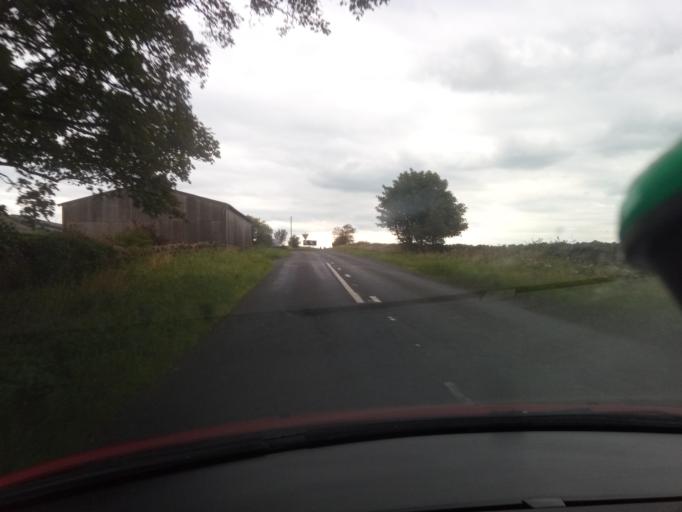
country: GB
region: England
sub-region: Northumberland
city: Bardon Mill
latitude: 54.9426
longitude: -2.2404
